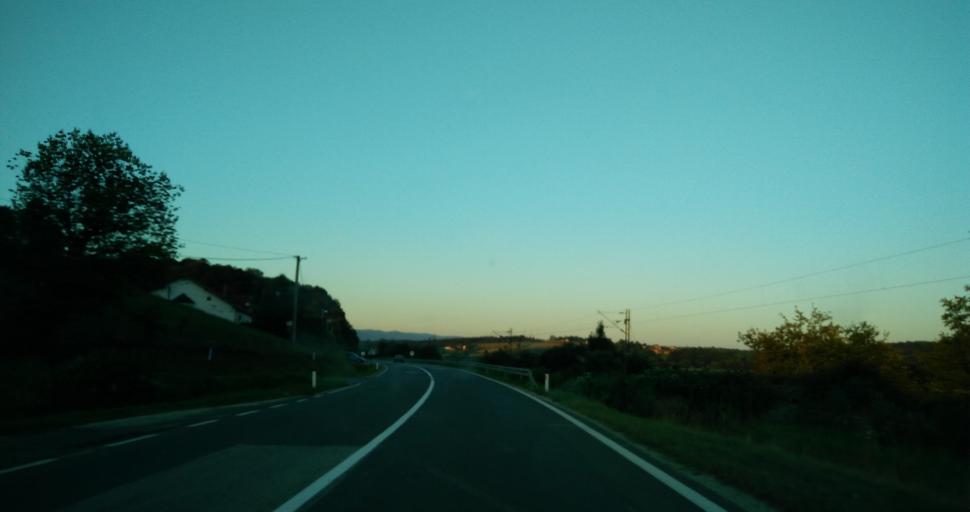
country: BA
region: Republika Srpska
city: Svodna
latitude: 45.0101
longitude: 16.5959
